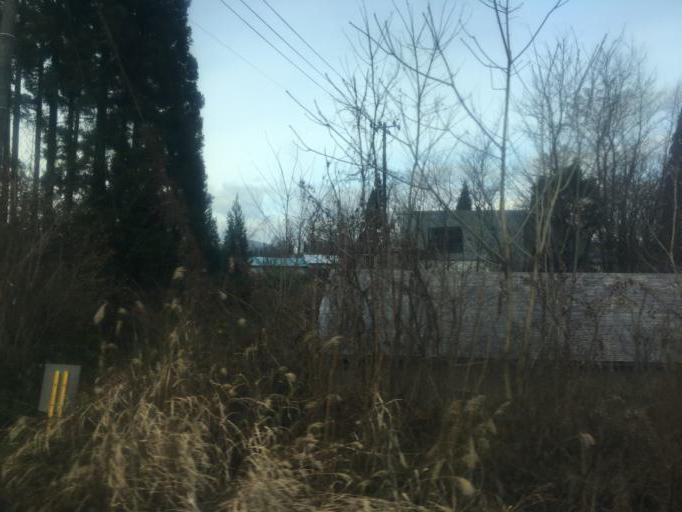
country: JP
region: Akita
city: Odate
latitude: 40.3103
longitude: 140.5732
